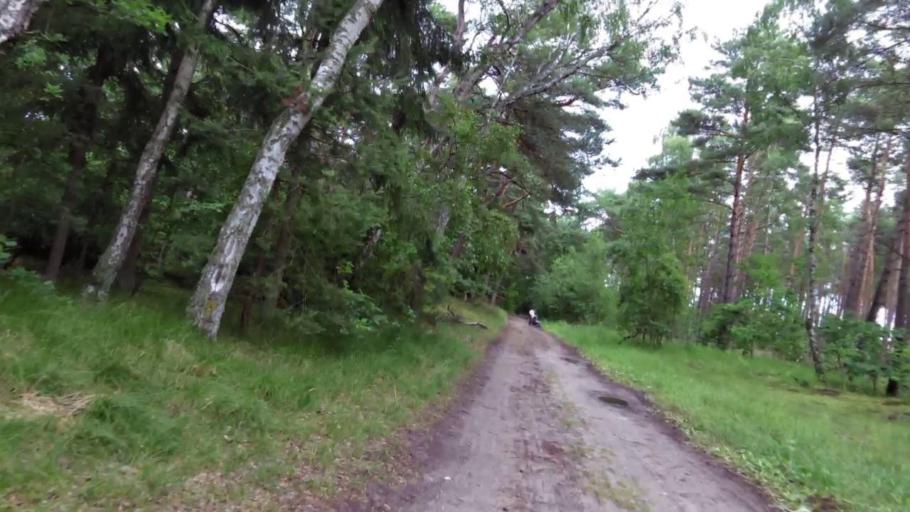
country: PL
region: West Pomeranian Voivodeship
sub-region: Powiat slawienski
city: Darlowo
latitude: 54.5058
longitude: 16.4637
